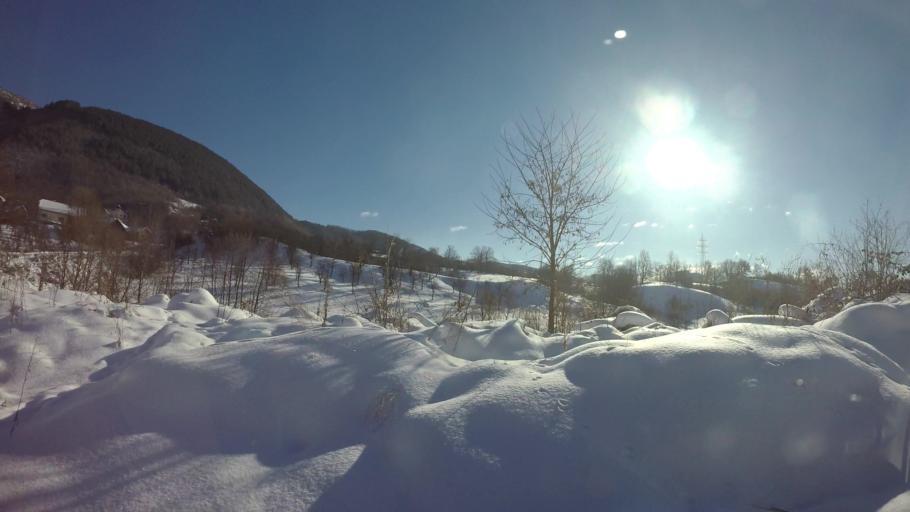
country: BA
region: Federation of Bosnia and Herzegovina
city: Kobilja Glava
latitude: 43.8975
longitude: 18.4123
